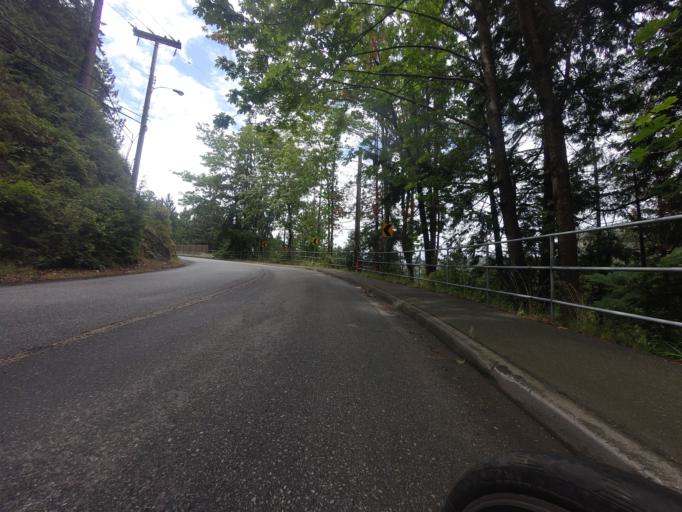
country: CA
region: British Columbia
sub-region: Greater Vancouver Regional District
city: Bowen Island
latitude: 49.3524
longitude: -123.2635
